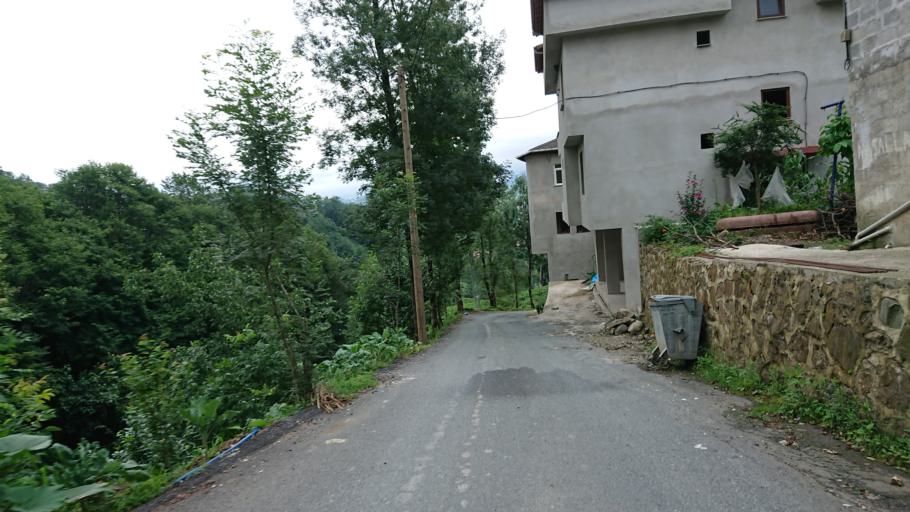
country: TR
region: Rize
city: Rize
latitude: 40.9661
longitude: 40.5116
